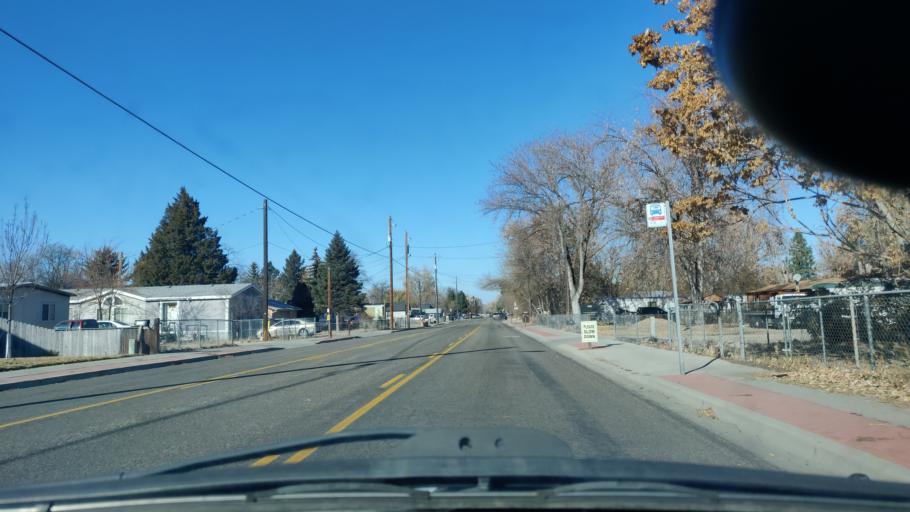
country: US
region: Idaho
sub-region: Ada County
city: Garden City
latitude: 43.6396
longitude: -116.2542
